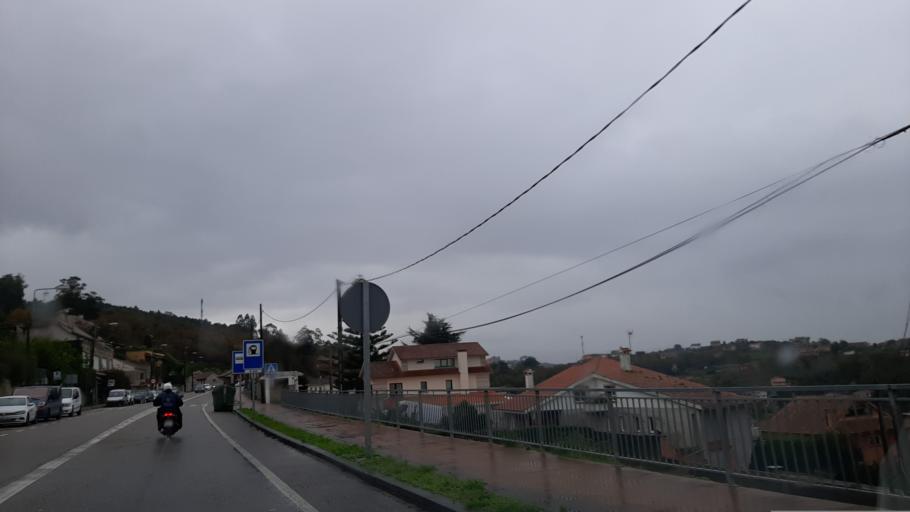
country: ES
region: Galicia
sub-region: Provincia de Pontevedra
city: Nigran
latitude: 42.1761
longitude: -8.7996
